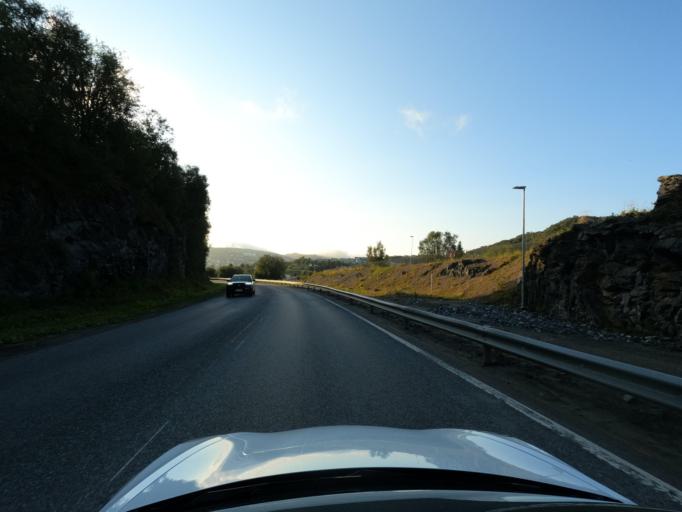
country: NO
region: Troms
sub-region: Harstad
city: Harstad
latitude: 68.7826
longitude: 16.5636
